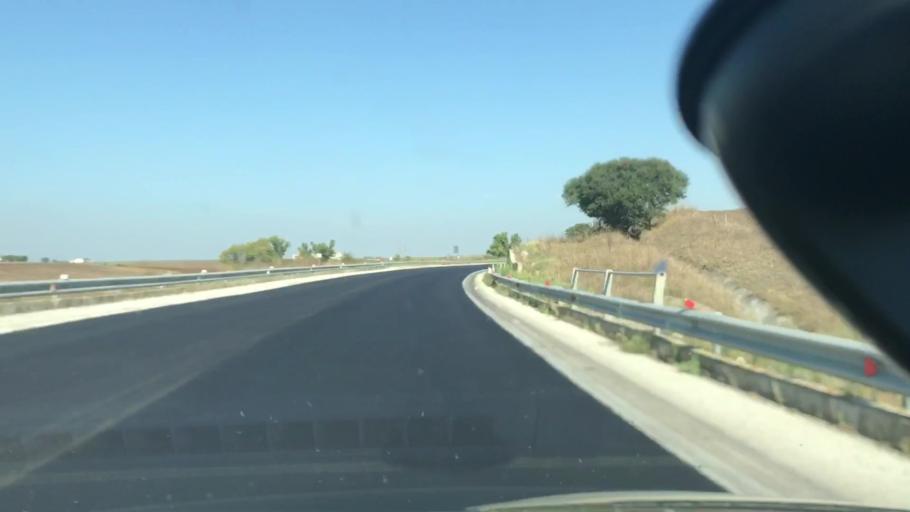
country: IT
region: Apulia
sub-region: Provincia di Barletta - Andria - Trani
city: Spinazzola
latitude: 40.9076
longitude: 16.1091
